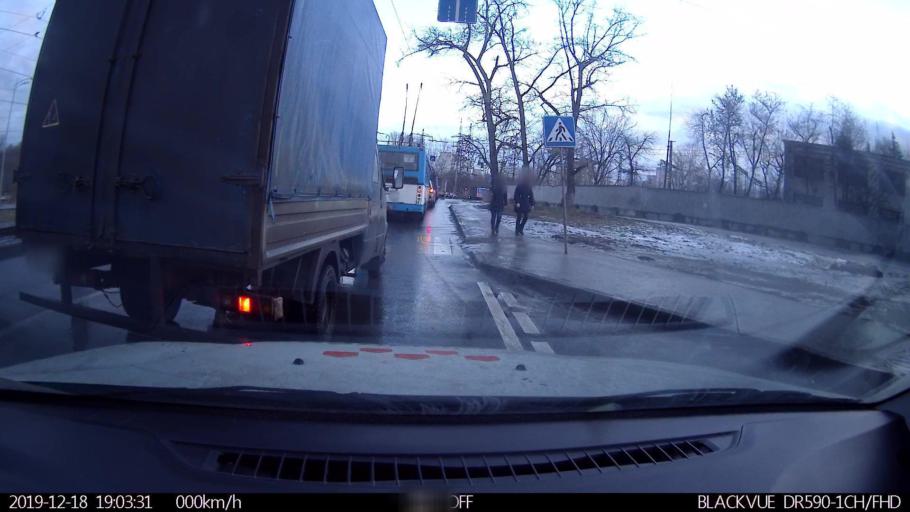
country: RU
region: Nizjnij Novgorod
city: Gorbatovka
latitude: 56.3313
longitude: 43.8602
